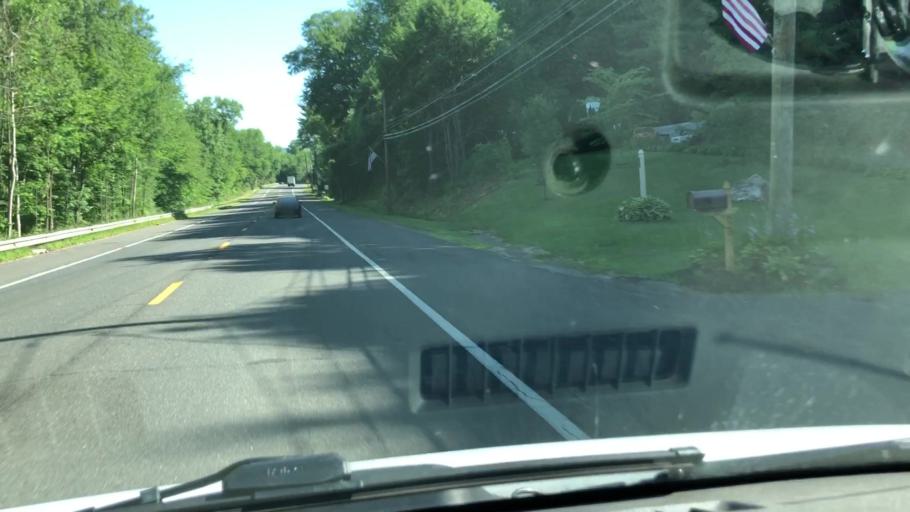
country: US
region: Massachusetts
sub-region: Berkshire County
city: Lanesborough
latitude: 42.5035
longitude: -73.1954
